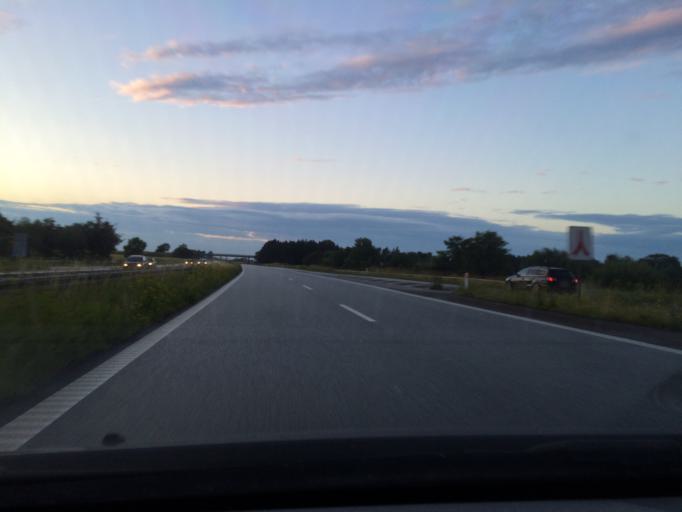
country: DK
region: Zealand
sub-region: Koge Kommune
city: Bjaeverskov
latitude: 55.3875
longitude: 12.0950
